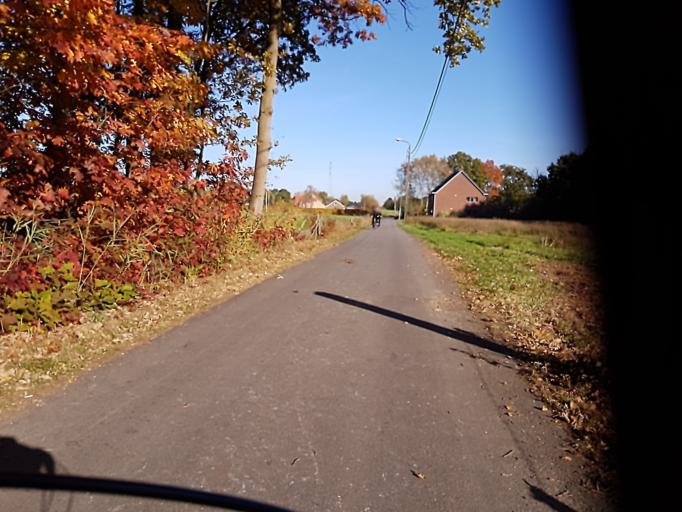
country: BE
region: Flanders
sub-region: Provincie Antwerpen
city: Sint-Katelijne-Waver
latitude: 51.0806
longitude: 4.5339
